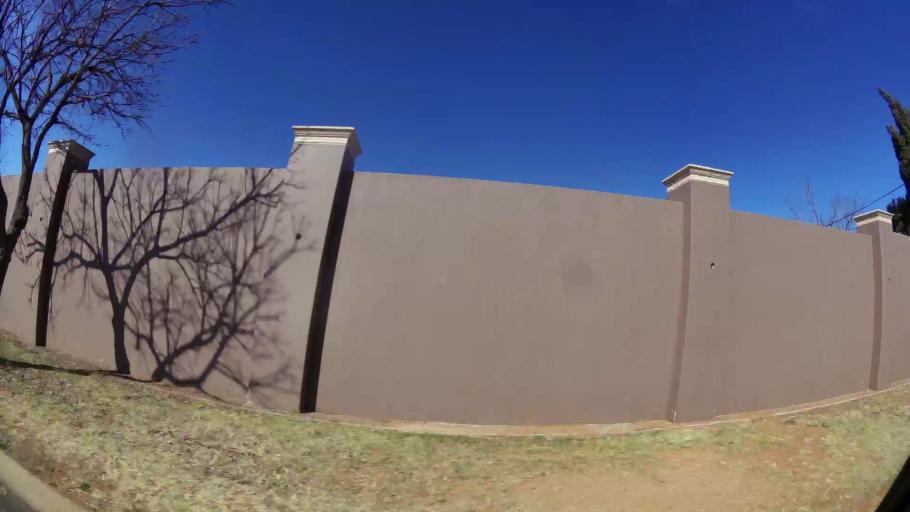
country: ZA
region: Gauteng
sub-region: City of Johannesburg Metropolitan Municipality
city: Johannesburg
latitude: -26.2885
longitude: 28.0486
